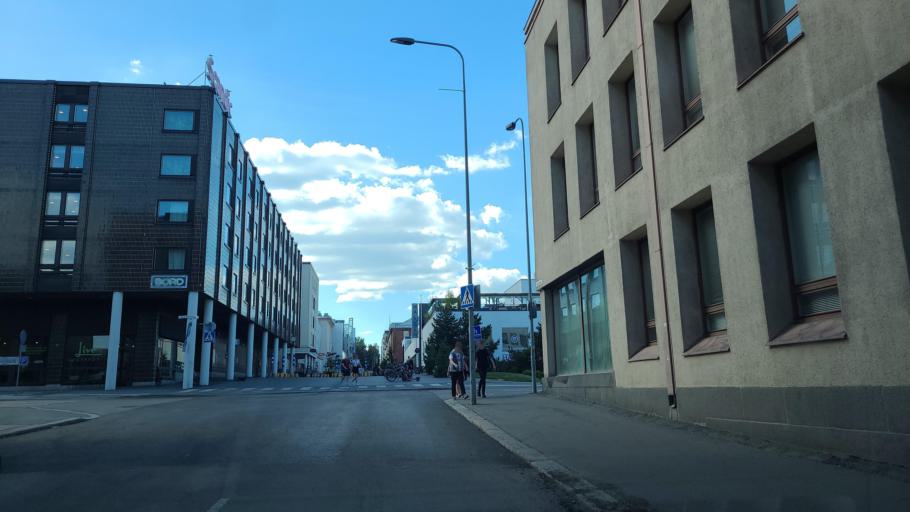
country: FI
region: Central Finland
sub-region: Jyvaeskylae
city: Jyvaeskylae
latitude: 62.2425
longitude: 25.7524
